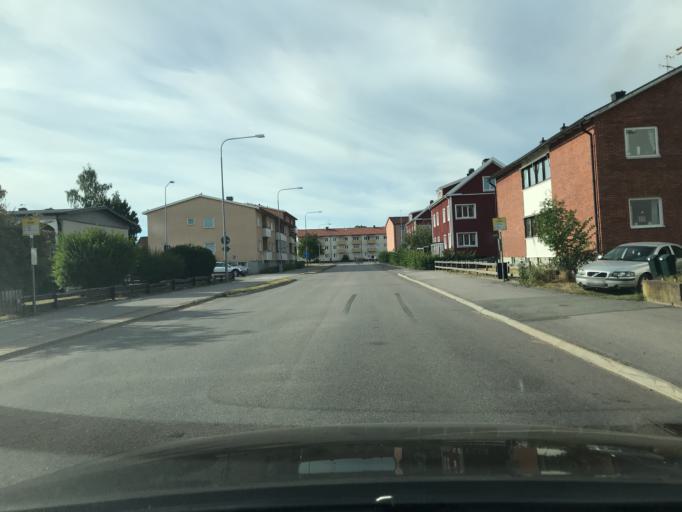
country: SE
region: Kalmar
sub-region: Hultsfreds Kommun
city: Hultsfred
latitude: 57.4902
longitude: 15.8406
